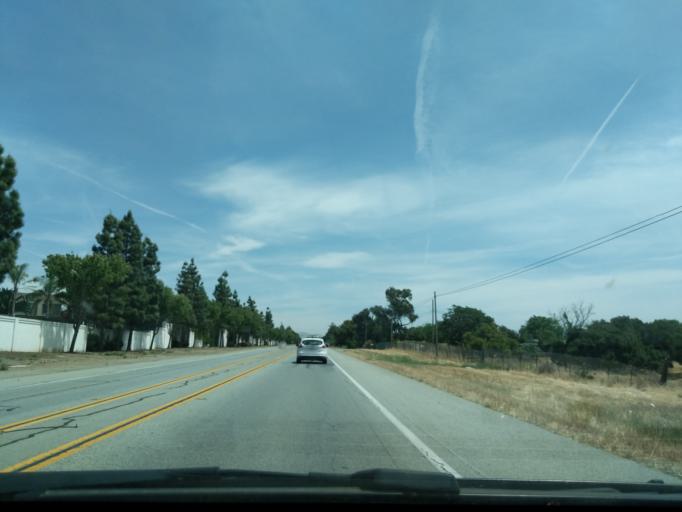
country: US
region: California
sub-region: San Benito County
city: Ridgemark
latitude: 36.8237
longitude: -121.3782
